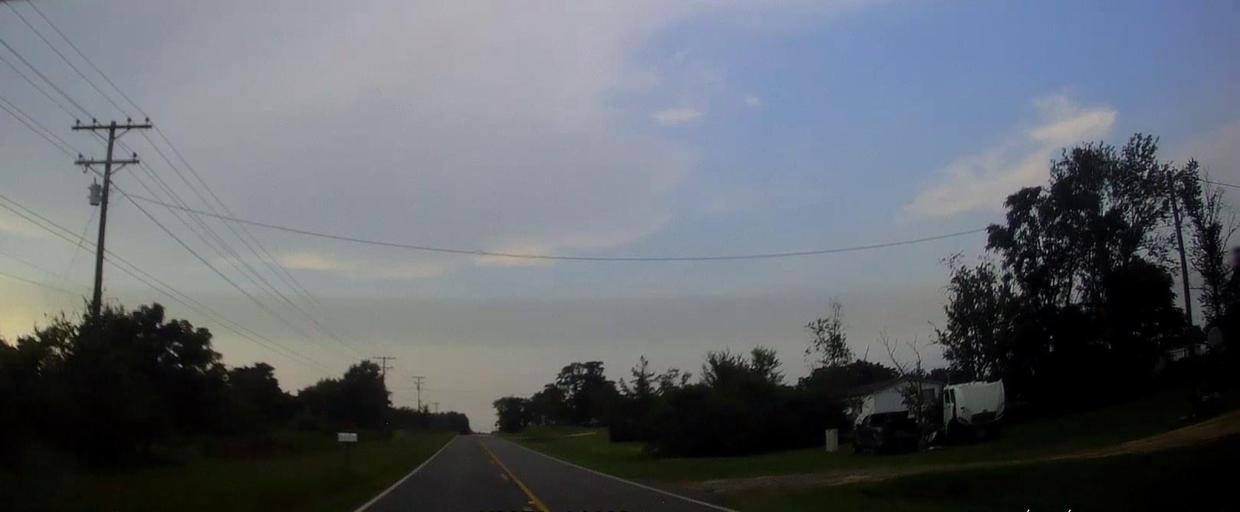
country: US
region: Georgia
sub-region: Laurens County
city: East Dublin
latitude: 32.5507
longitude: -82.8375
